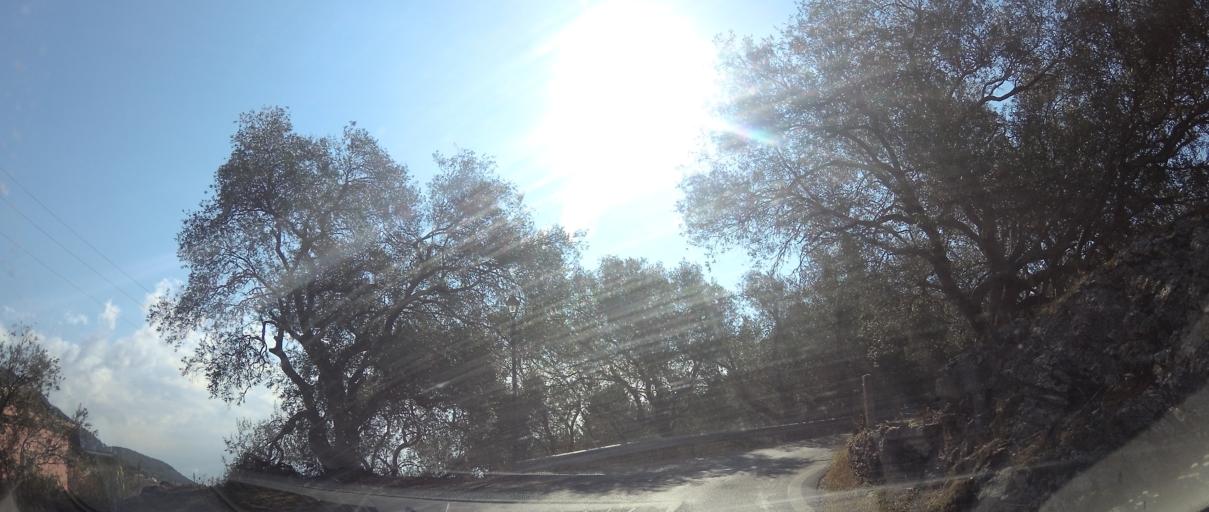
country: GR
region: Ionian Islands
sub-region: Nomos Kerkyras
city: Acharavi
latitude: 39.7206
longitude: 19.8380
